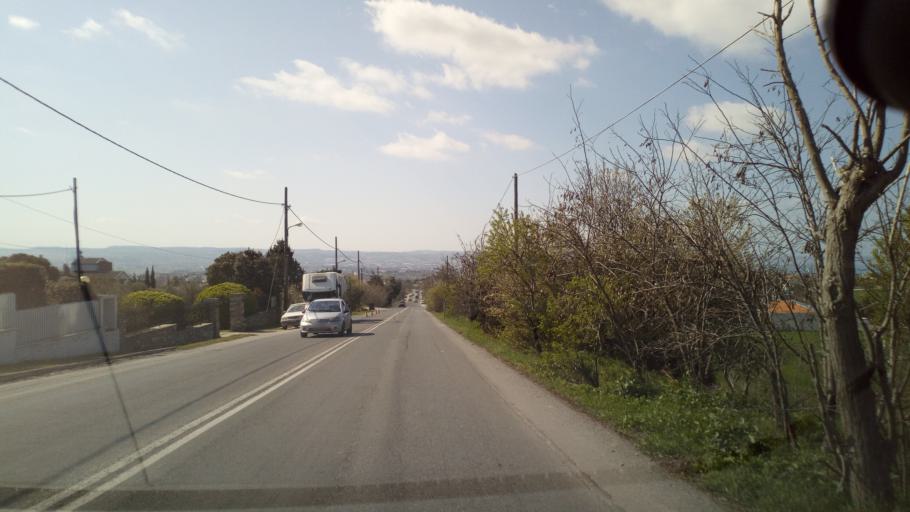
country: GR
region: Central Macedonia
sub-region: Nomos Thessalonikis
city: Thermi
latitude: 40.5621
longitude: 23.0236
